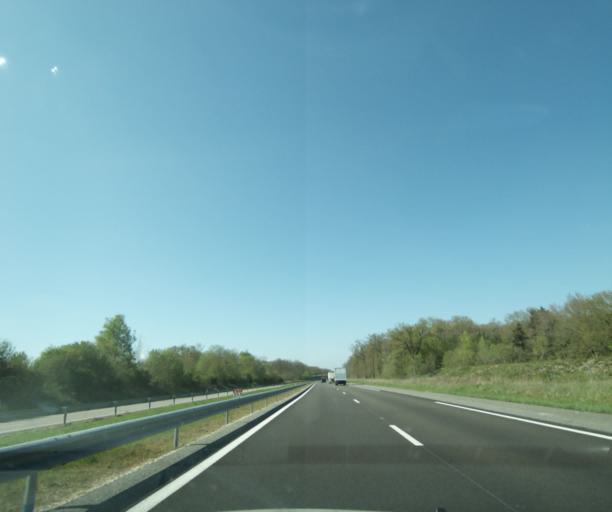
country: FR
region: Bourgogne
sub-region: Departement de la Nievre
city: Neuvy-sur-Loire
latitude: 47.4937
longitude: 2.9336
